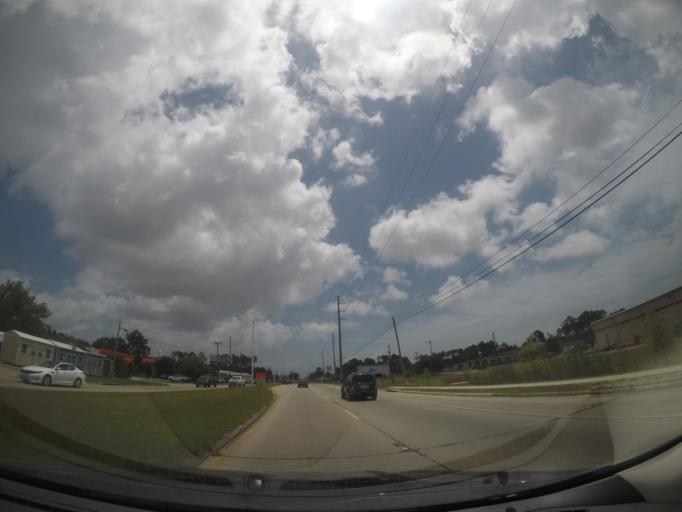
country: US
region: Mississippi
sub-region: Hancock County
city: Waveland
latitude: 30.3107
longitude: -89.3646
